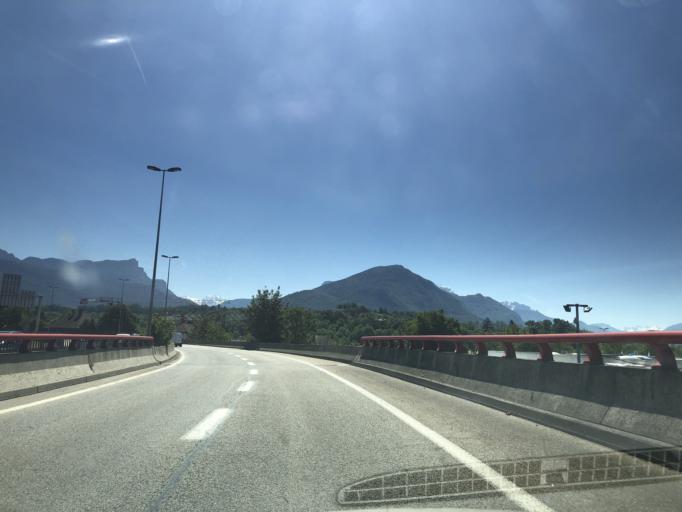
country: FR
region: Rhone-Alpes
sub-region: Departement de la Haute-Savoie
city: Pringy
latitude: 45.9352
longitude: 6.1208
